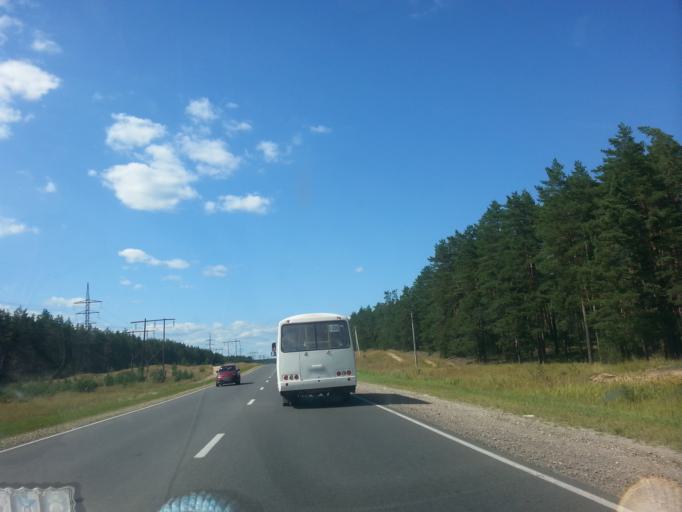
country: RU
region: Nizjnij Novgorod
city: Lukino
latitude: 56.3949
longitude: 43.6800
